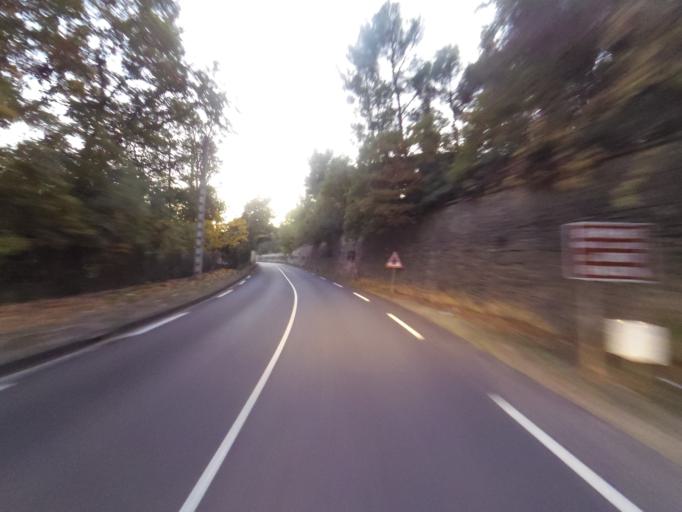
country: FR
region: Provence-Alpes-Cote d'Azur
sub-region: Departement du Vaucluse
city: Carpentras
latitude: 44.0633
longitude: 5.0607
